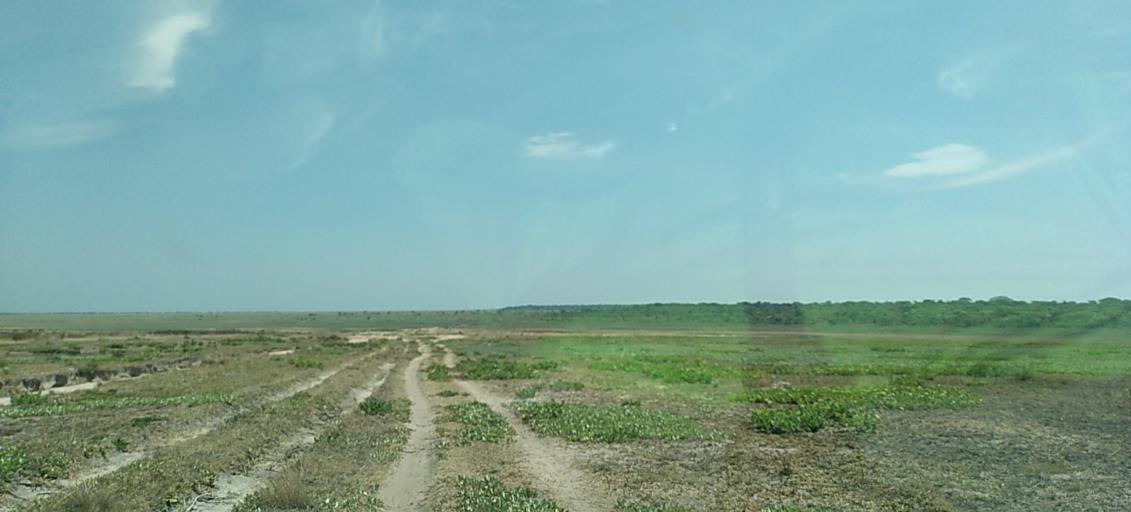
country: ZM
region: North-Western
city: Mwinilunga
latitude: -11.6717
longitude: 25.2067
